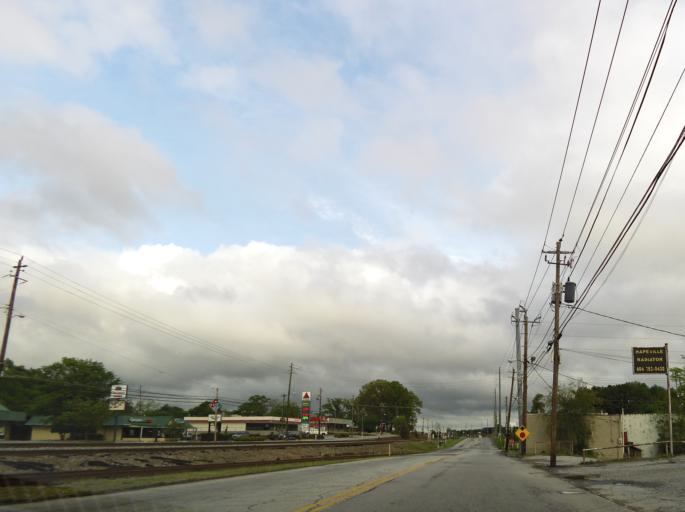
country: US
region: Georgia
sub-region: Fulton County
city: Hapeville
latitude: 33.6572
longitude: -84.4068
